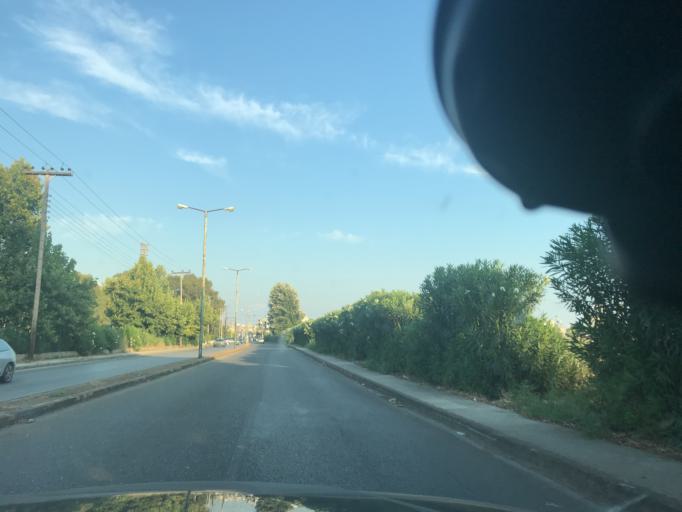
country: GR
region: West Greece
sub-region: Nomos Ileias
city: Pyrgos
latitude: 37.6797
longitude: 21.4240
